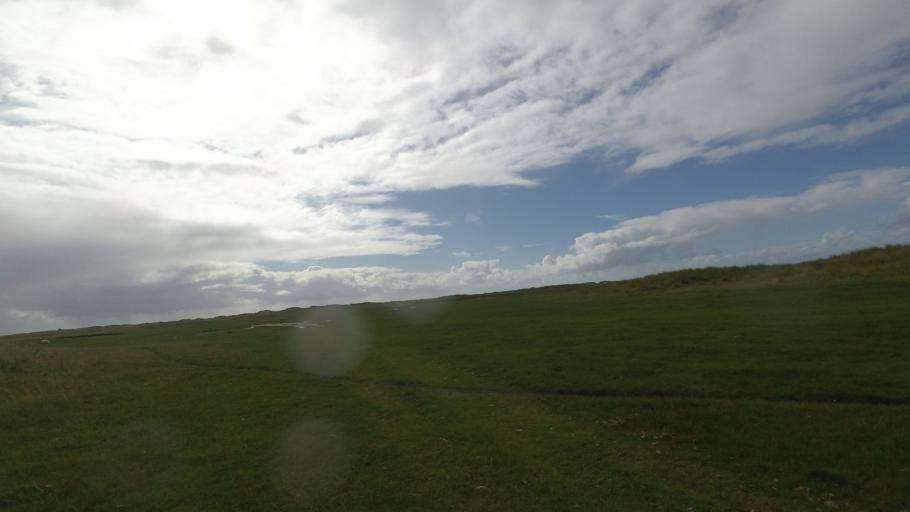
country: NL
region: Friesland
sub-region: Gemeente Ameland
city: Nes
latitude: 53.4551
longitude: 5.8641
